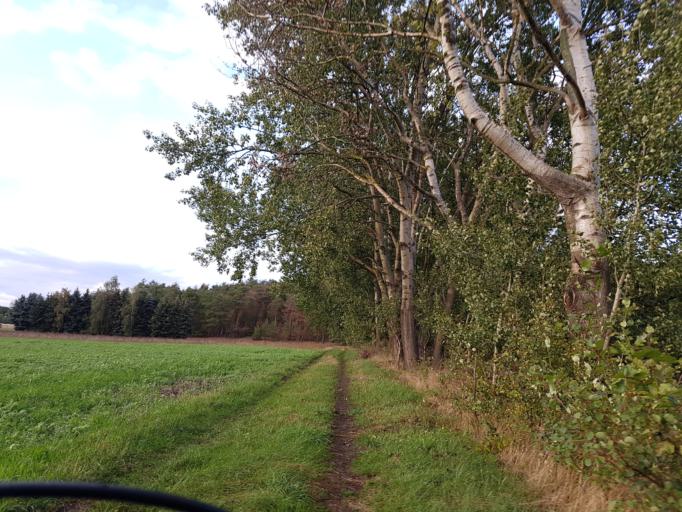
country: DE
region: Brandenburg
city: Bad Liebenwerda
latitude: 51.5433
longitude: 13.4266
